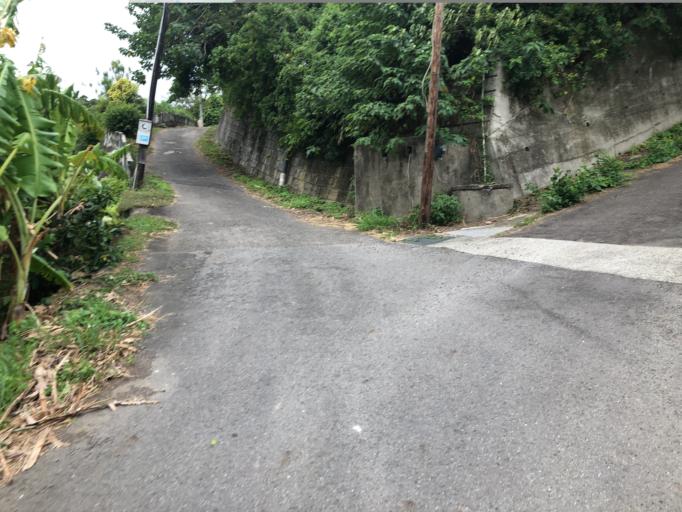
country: TW
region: Taiwan
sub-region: Hsinchu
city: Hsinchu
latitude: 24.7539
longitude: 120.9479
